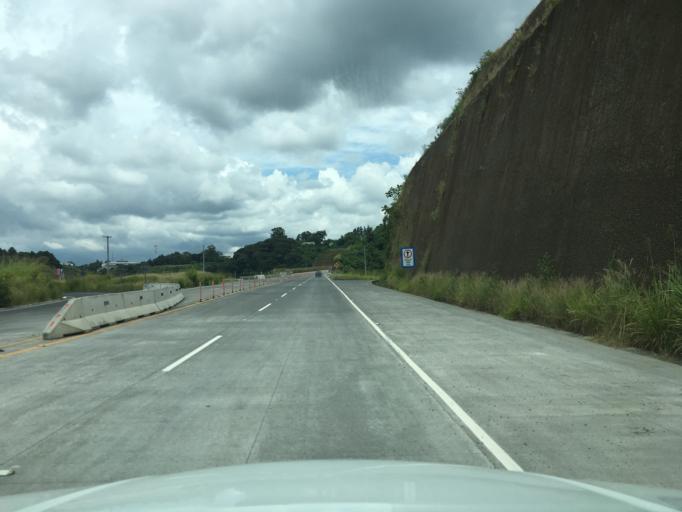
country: GT
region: Guatemala
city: Petapa
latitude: 14.5009
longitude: -90.5442
